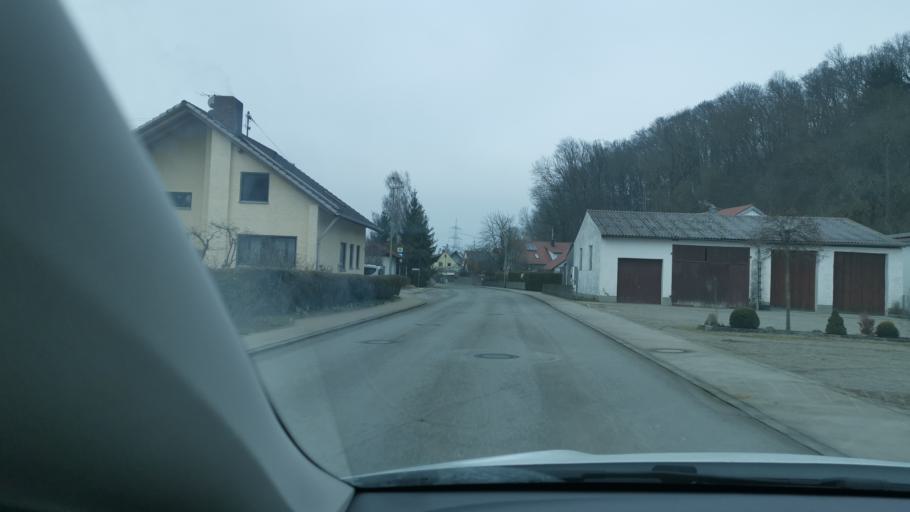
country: DE
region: Bavaria
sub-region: Swabia
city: Rehling
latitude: 48.4942
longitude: 10.9215
